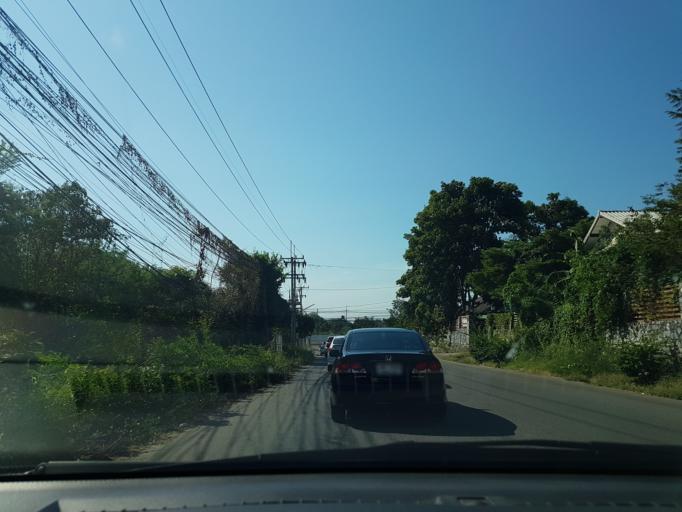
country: TH
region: Chon Buri
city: Sattahip
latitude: 12.6665
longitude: 100.9275
